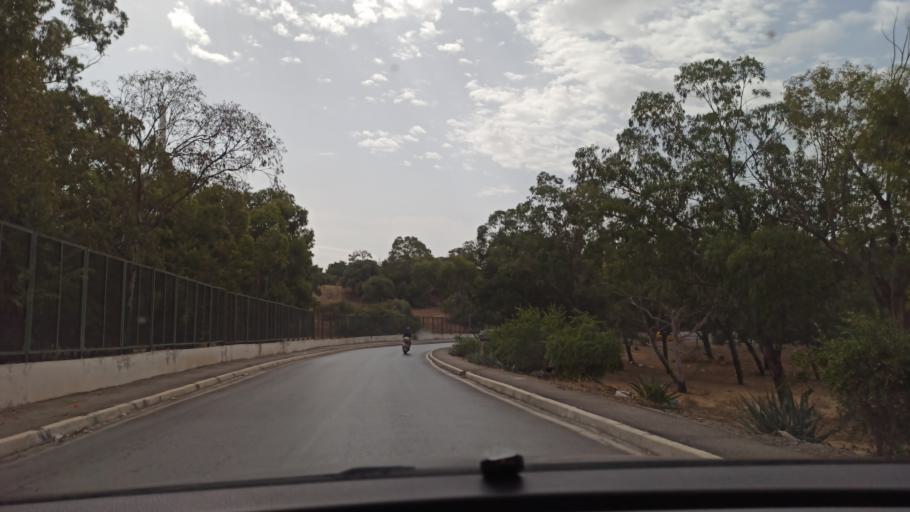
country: TN
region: Tunis
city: Tunis
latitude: 36.8257
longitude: 10.1685
